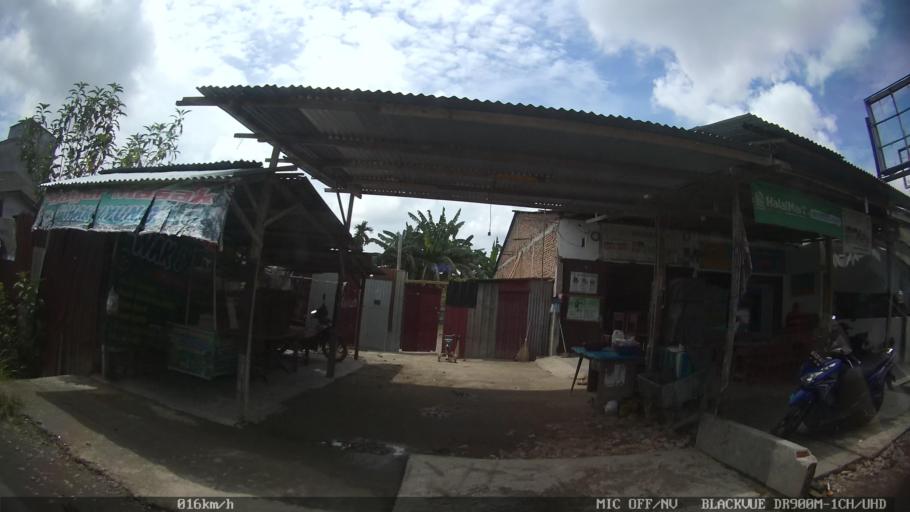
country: ID
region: North Sumatra
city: Medan
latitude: 3.6072
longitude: 98.7515
